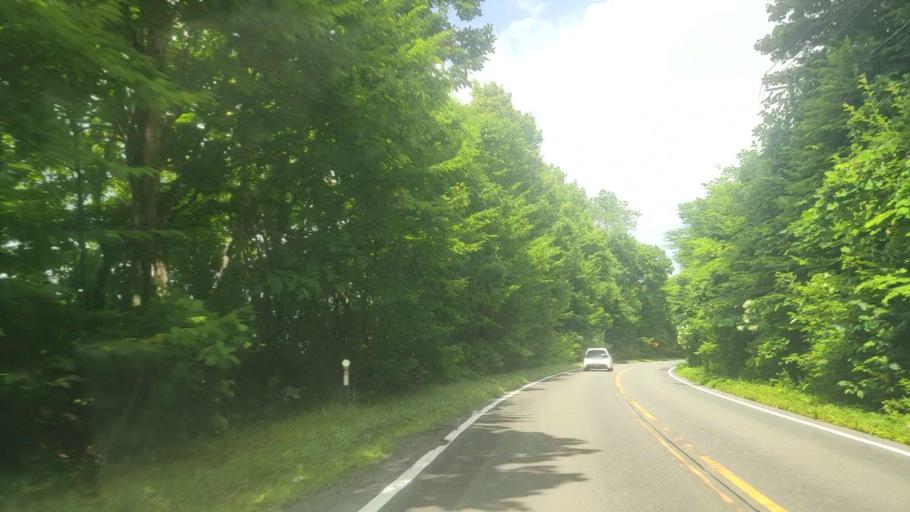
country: JP
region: Hokkaido
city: Date
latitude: 42.5619
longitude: 140.8779
